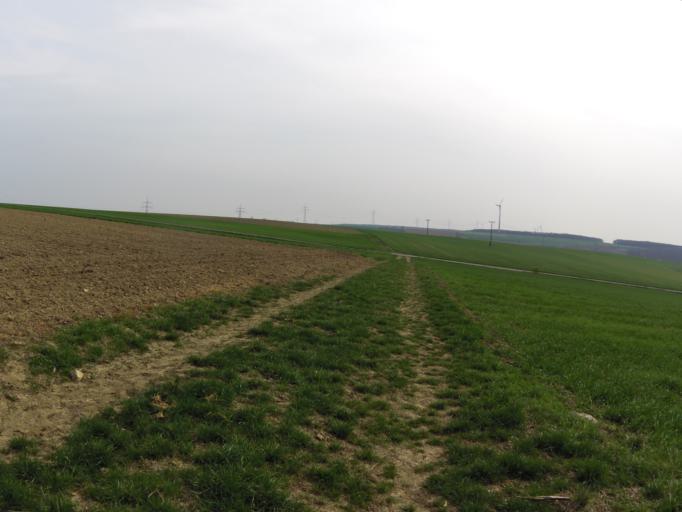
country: DE
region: Bavaria
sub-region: Regierungsbezirk Unterfranken
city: Theilheim
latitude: 49.7640
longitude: 10.0421
